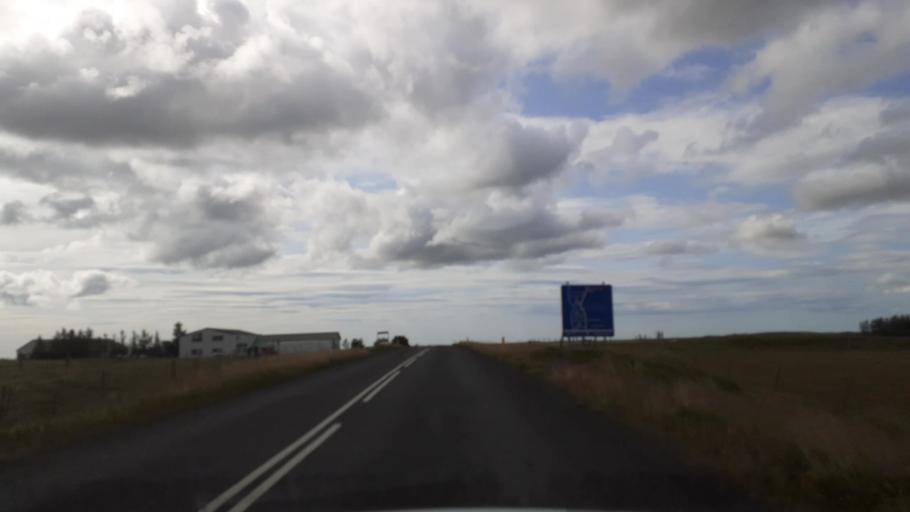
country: IS
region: South
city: Vestmannaeyjar
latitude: 63.8380
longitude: -20.4134
